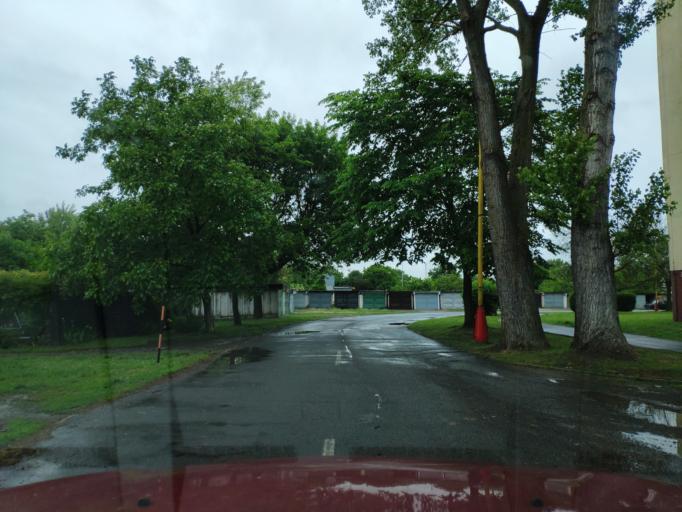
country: SK
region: Kosicky
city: Cierna nad Tisou
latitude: 48.4153
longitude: 22.0813
